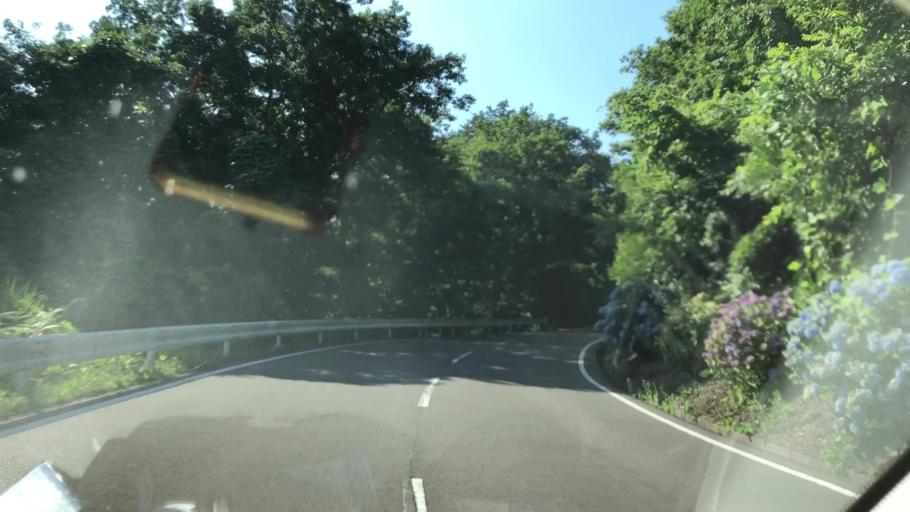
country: JP
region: Miyagi
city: Shiroishi
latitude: 38.0198
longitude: 140.5705
